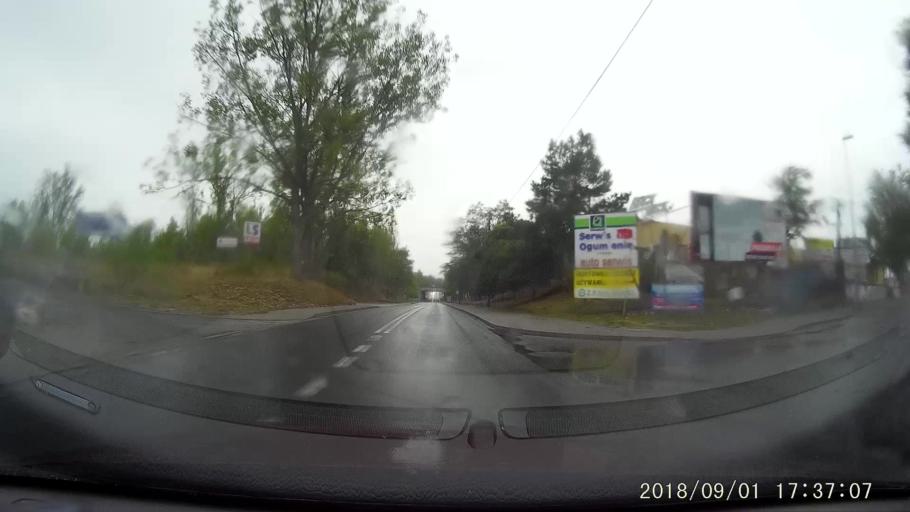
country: PL
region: Lubusz
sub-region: Powiat zaganski
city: Zagan
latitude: 51.6099
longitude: 15.3023
